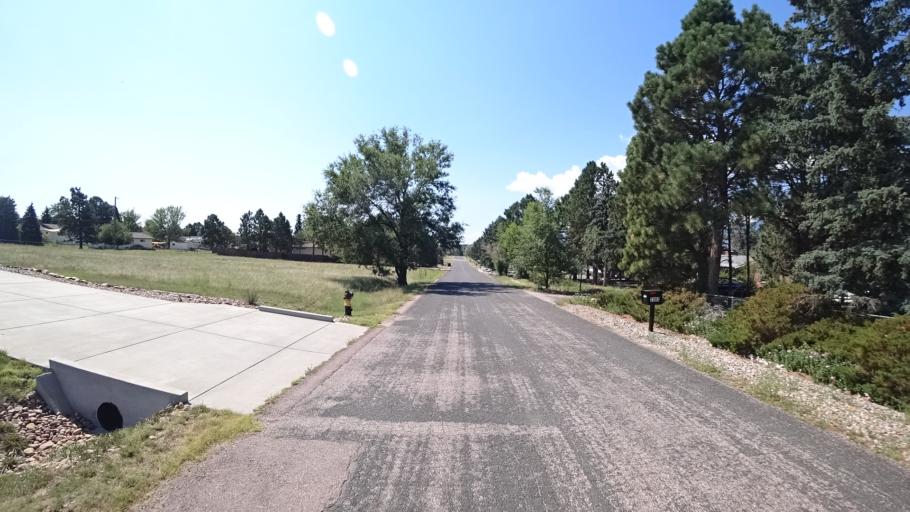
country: US
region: Colorado
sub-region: El Paso County
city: Air Force Academy
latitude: 38.9384
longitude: -104.7893
